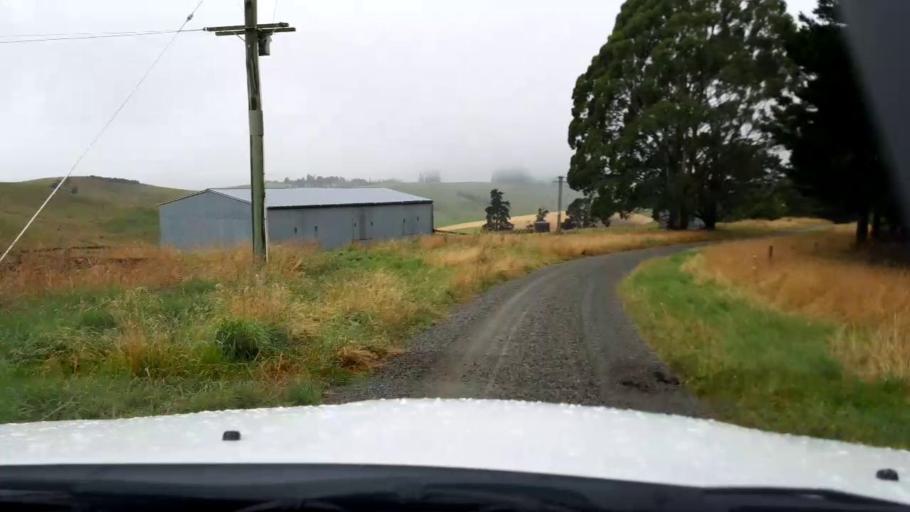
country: NZ
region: Canterbury
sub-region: Timaru District
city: Pleasant Point
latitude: -44.1778
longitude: 171.0962
